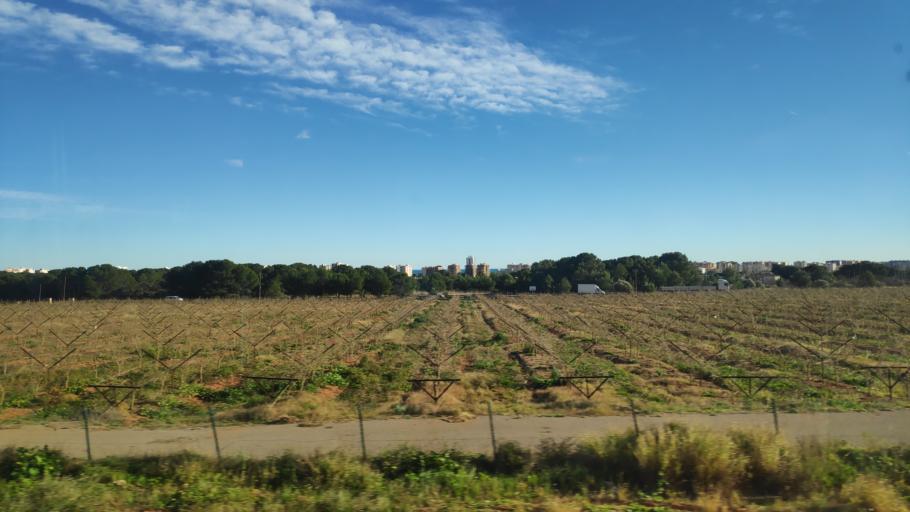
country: ES
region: Valencia
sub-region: Provincia de Castello
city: Benicassim
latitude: 40.0413
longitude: 0.0342
